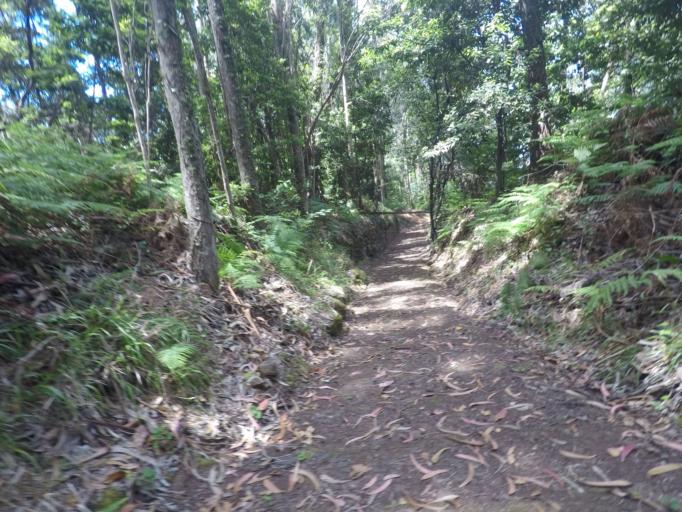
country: PT
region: Madeira
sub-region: Porto Moniz
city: Porto Moniz
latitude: 32.8419
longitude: -17.1487
